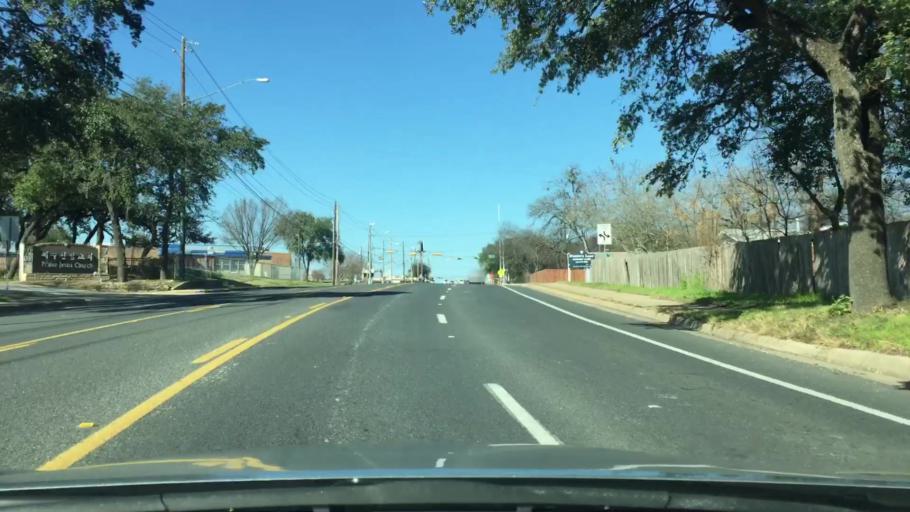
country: US
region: Texas
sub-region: Travis County
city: Wells Branch
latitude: 30.3794
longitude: -97.6821
